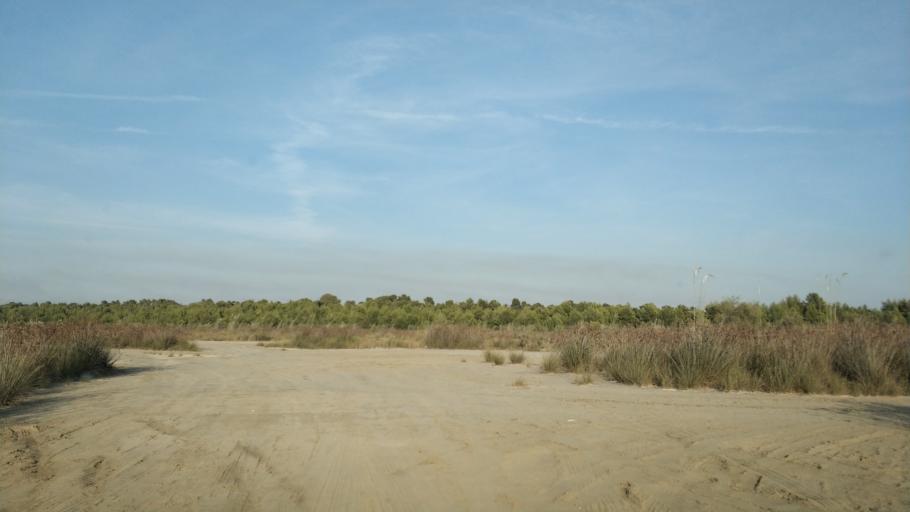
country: AL
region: Fier
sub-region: Rrethi i Lushnjes
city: Divjake
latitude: 40.9565
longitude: 19.4705
